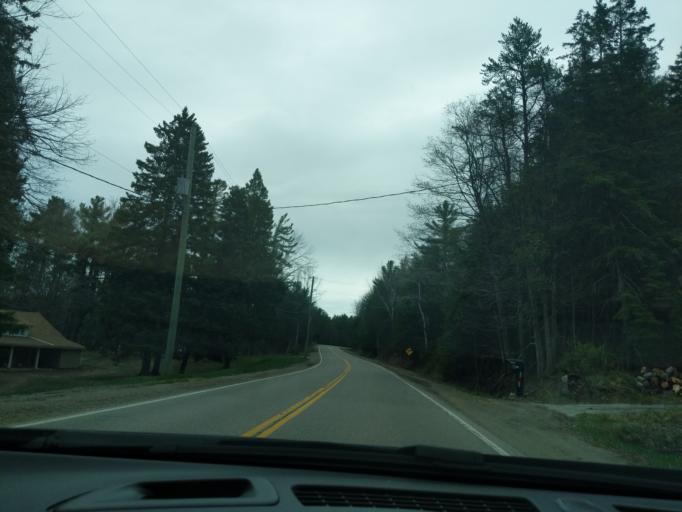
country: CA
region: Ontario
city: Orangeville
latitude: 43.9950
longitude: -80.0126
